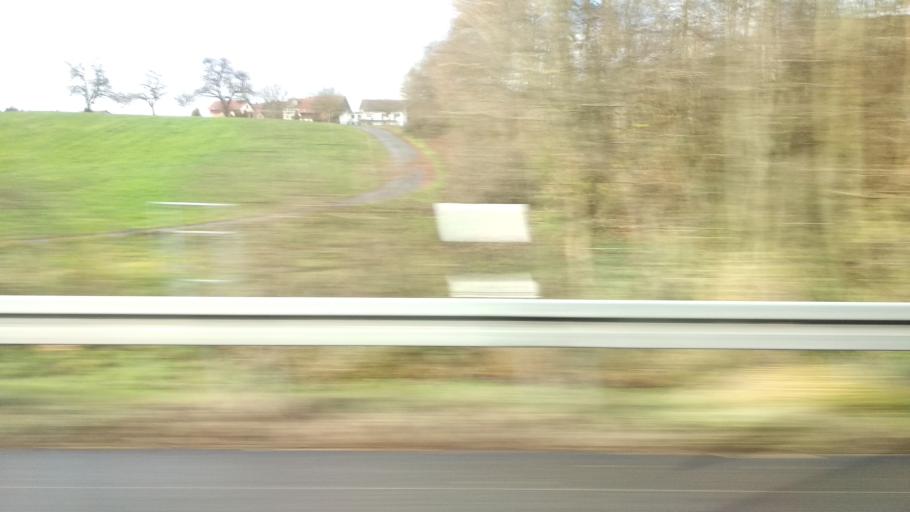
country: DE
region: Bavaria
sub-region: Swabia
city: Weissensberg
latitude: 47.6245
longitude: 9.7393
